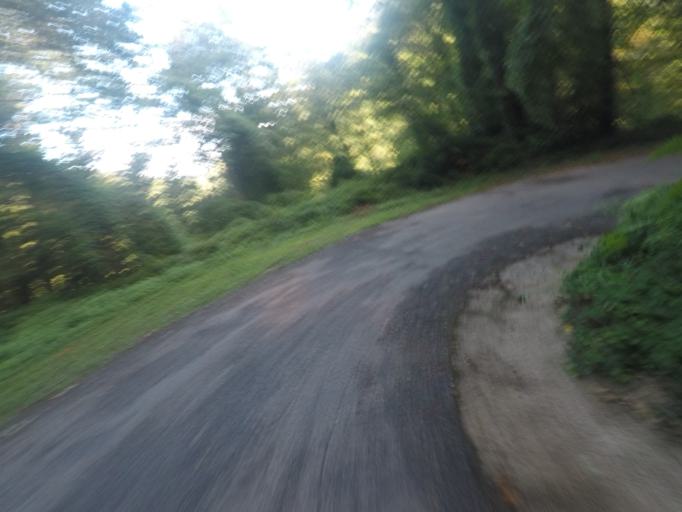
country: IT
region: Tuscany
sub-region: Provincia di Lucca
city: Pescaglia
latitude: 43.9415
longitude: 10.3944
